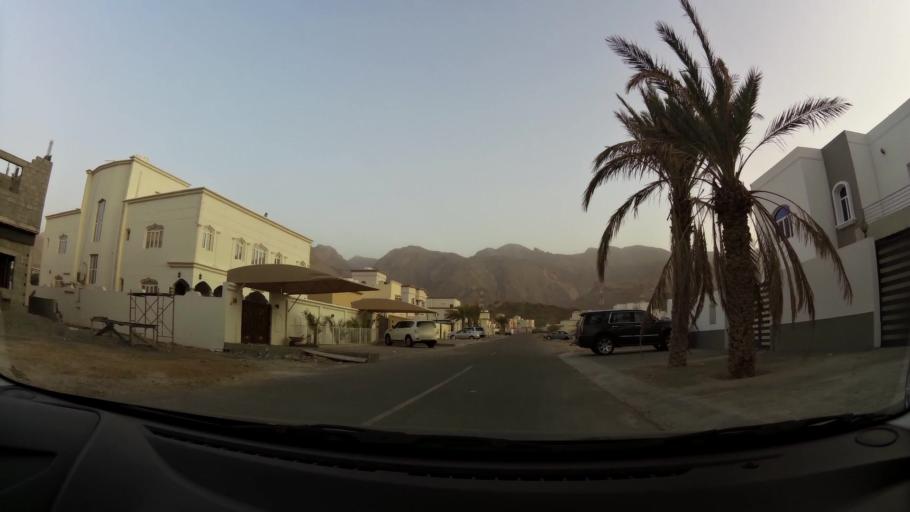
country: OM
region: Muhafazat Masqat
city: Bawshar
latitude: 23.4751
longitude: 58.3048
